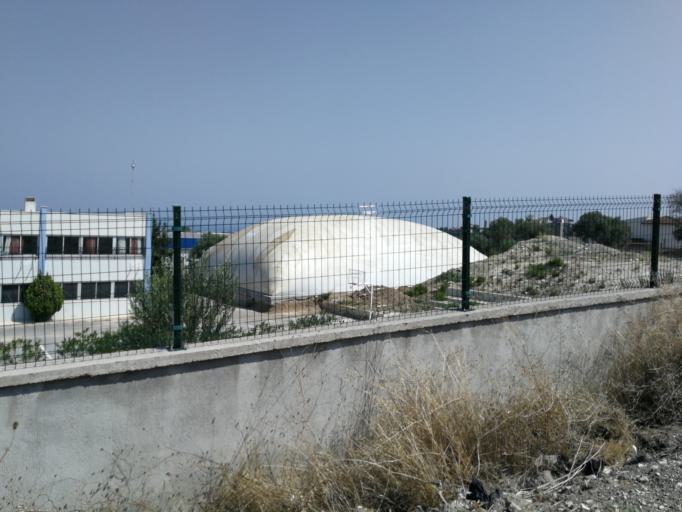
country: TR
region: Izmir
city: Urla
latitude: 38.3252
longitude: 26.7726
